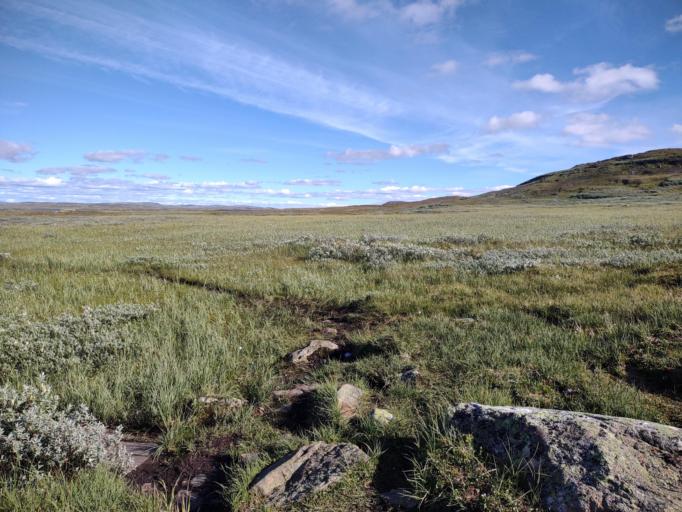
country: NO
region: Hordaland
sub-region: Eidfjord
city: Eidfjord
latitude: 60.1732
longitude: 7.4492
